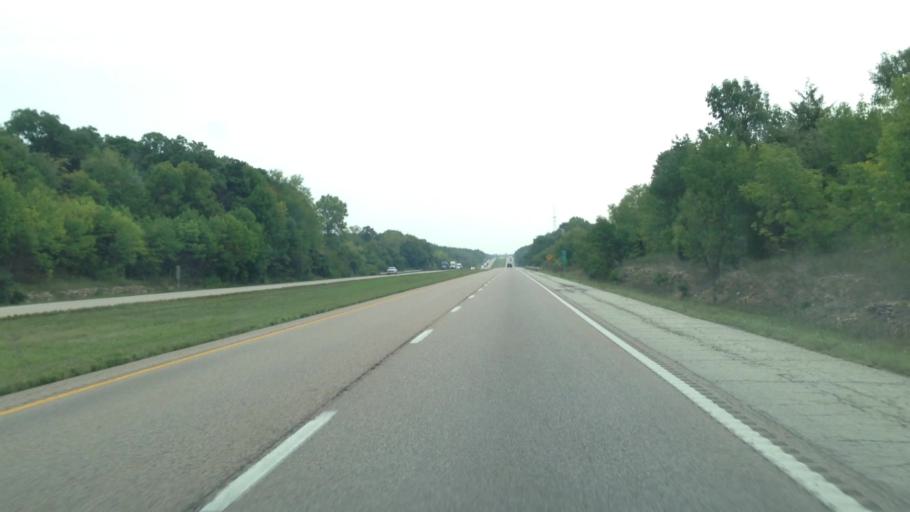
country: US
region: Missouri
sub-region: Clinton County
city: Lathrop
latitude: 39.4839
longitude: -94.3055
